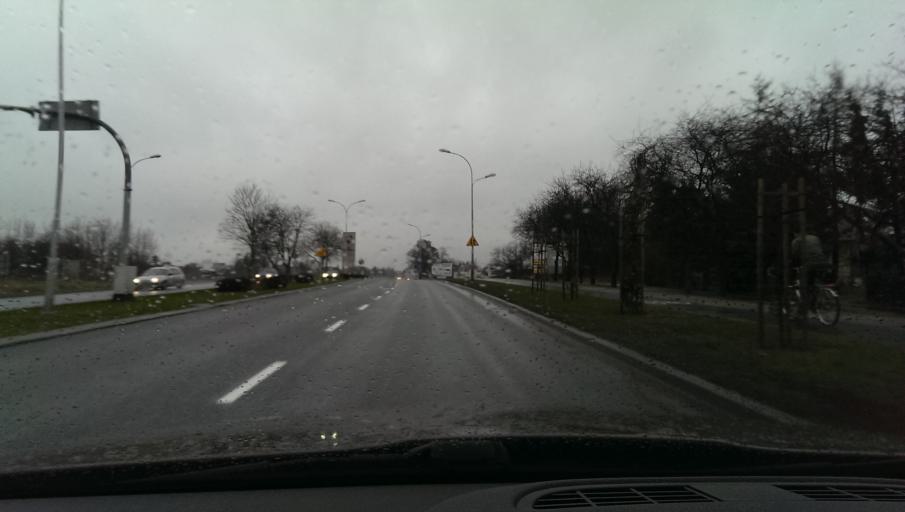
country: PL
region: Subcarpathian Voivodeship
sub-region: Rzeszow
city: Rzeszow
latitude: 50.0719
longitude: 21.9892
